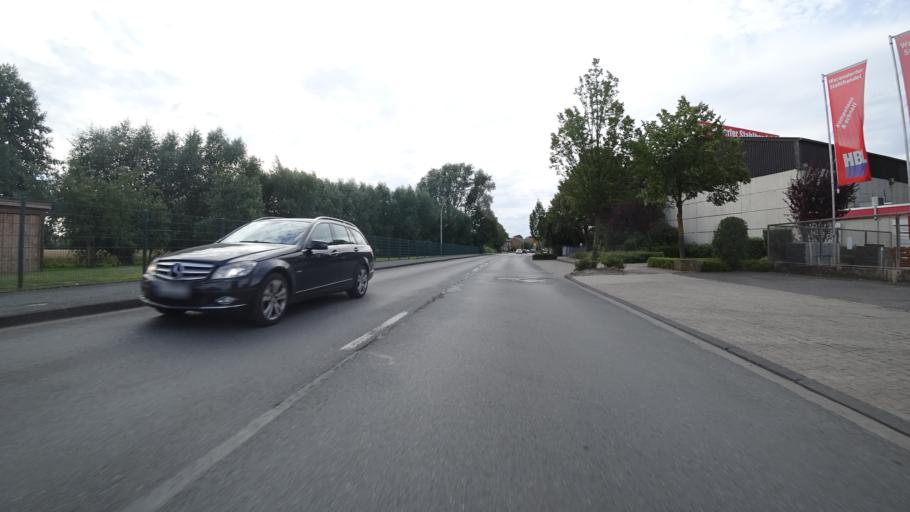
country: DE
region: North Rhine-Westphalia
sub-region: Regierungsbezirk Munster
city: Warendorf
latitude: 51.9450
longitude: 8.0029
